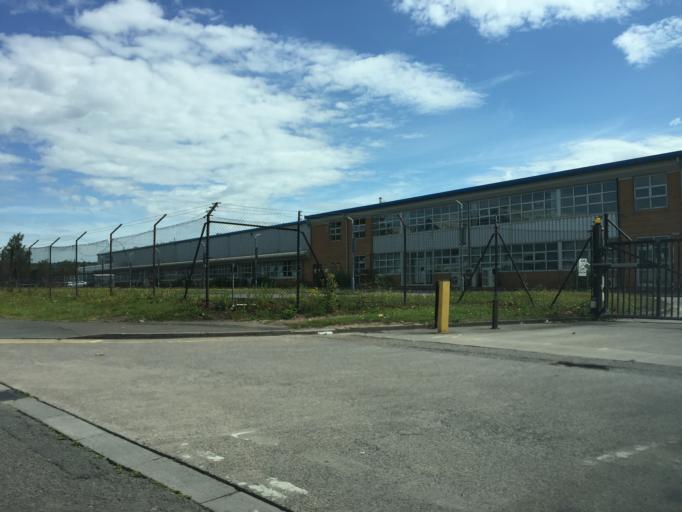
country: GB
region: Wales
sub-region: Newport
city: Nash
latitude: 51.5694
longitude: -2.9655
